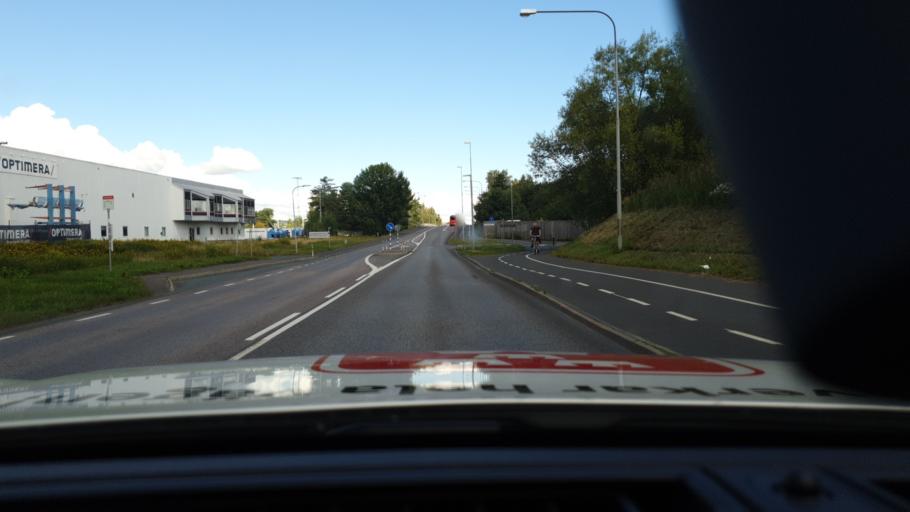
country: SE
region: Joenkoeping
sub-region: Jonkopings Kommun
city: Jonkoping
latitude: 57.7564
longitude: 14.1696
